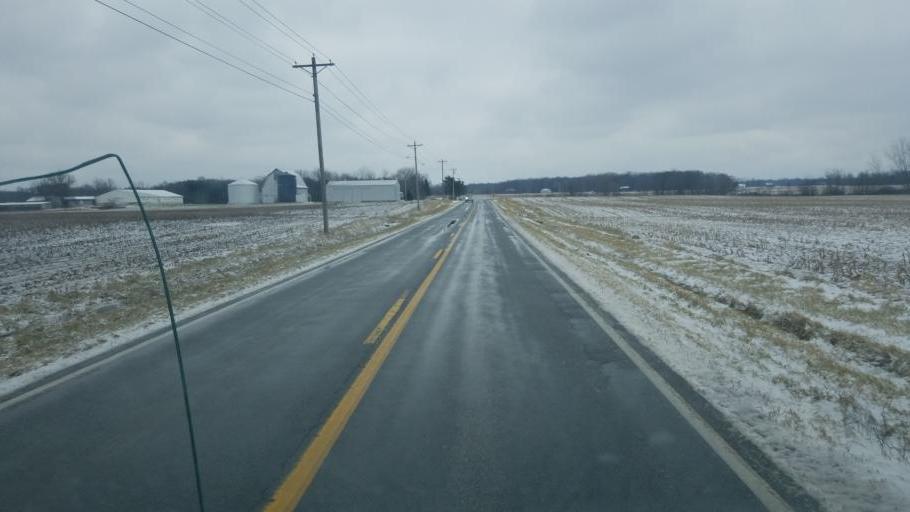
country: US
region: Ohio
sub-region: Delaware County
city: Sunbury
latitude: 40.3182
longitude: -82.8008
